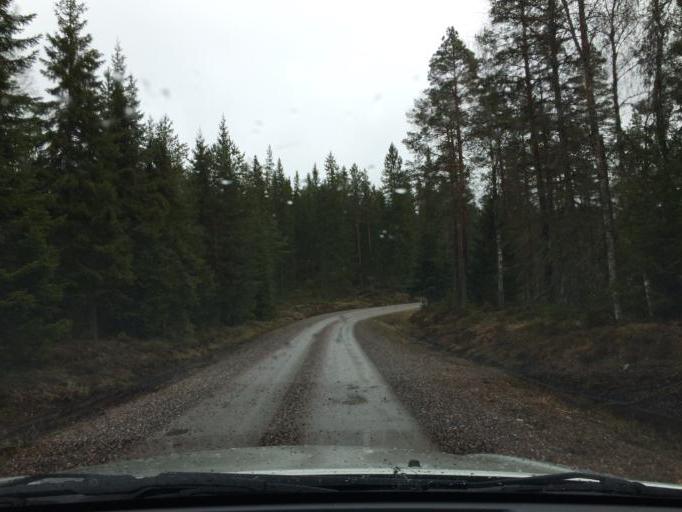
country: SE
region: OErebro
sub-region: Hallefors Kommun
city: Haellefors
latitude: 60.0224
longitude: 14.5648
